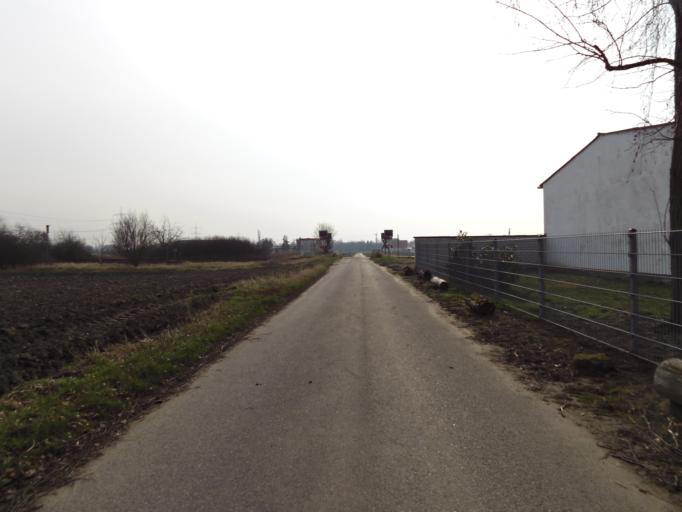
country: DE
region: Rheinland-Pfalz
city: Lambsheim
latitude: 49.5118
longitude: 8.3002
